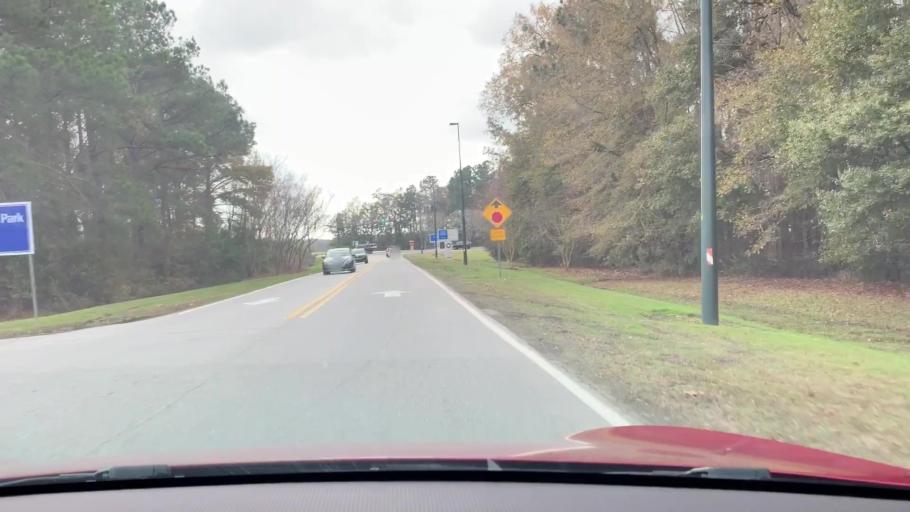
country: US
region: Georgia
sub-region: Chatham County
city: Pooler
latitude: 32.1355
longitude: -81.2146
